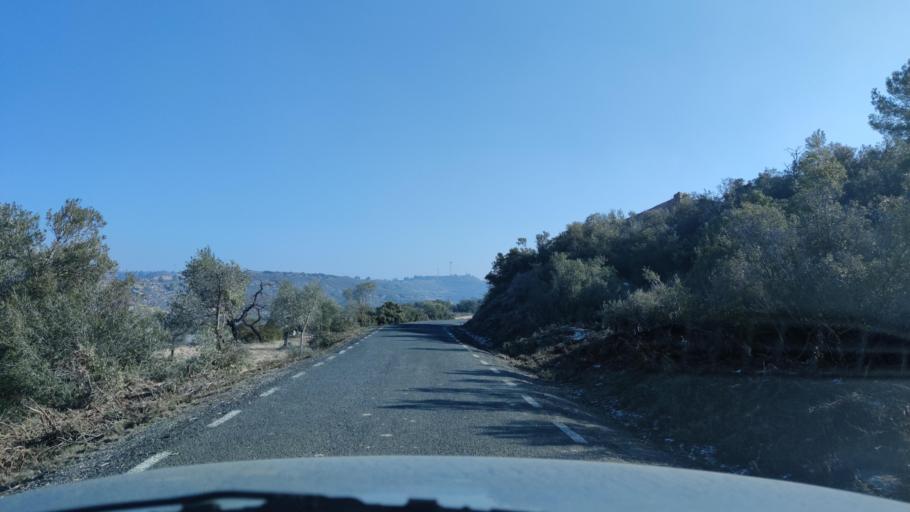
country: ES
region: Catalonia
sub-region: Provincia de Lleida
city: Torrebesses
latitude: 41.4304
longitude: 0.5822
